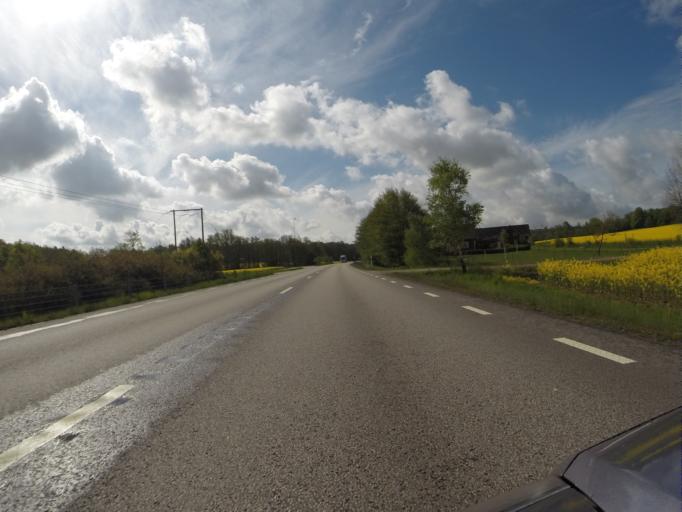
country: SE
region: Skane
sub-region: Bjuvs Kommun
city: Billesholm
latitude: 56.0443
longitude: 12.9684
